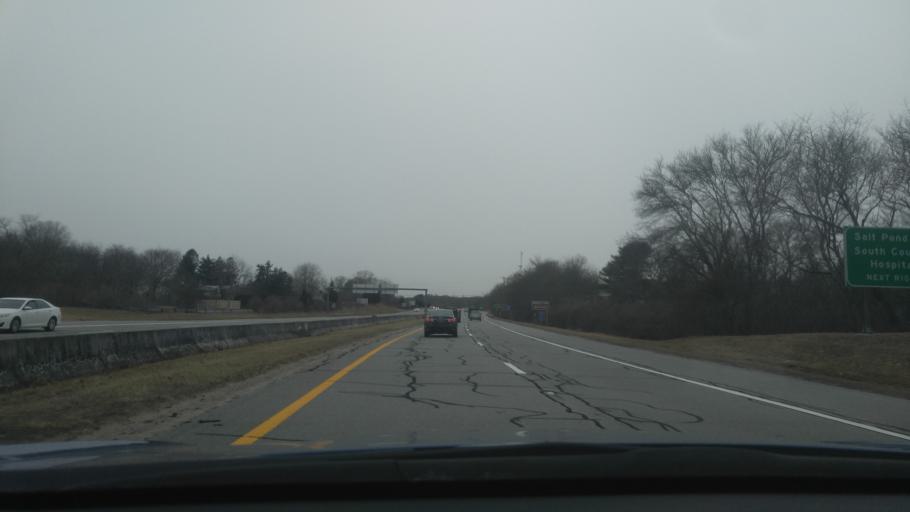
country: US
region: Rhode Island
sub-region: Washington County
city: Wakefield-Peacedale
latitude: 41.4304
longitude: -71.4876
